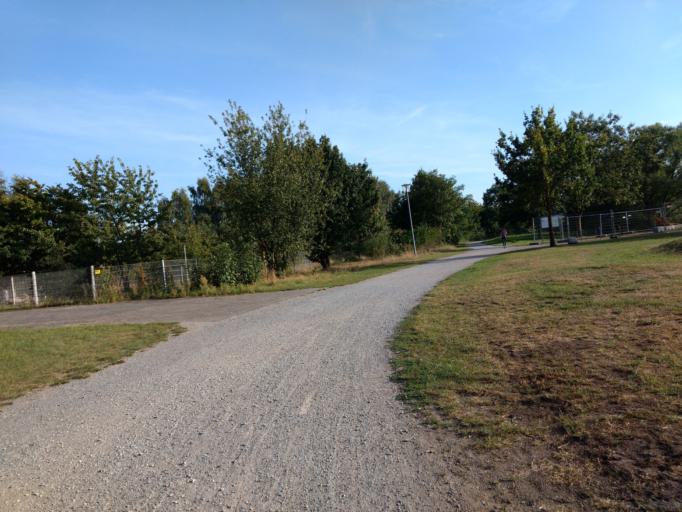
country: DE
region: North Rhine-Westphalia
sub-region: Regierungsbezirk Detmold
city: Hovelhof
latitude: 51.7608
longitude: 8.6884
